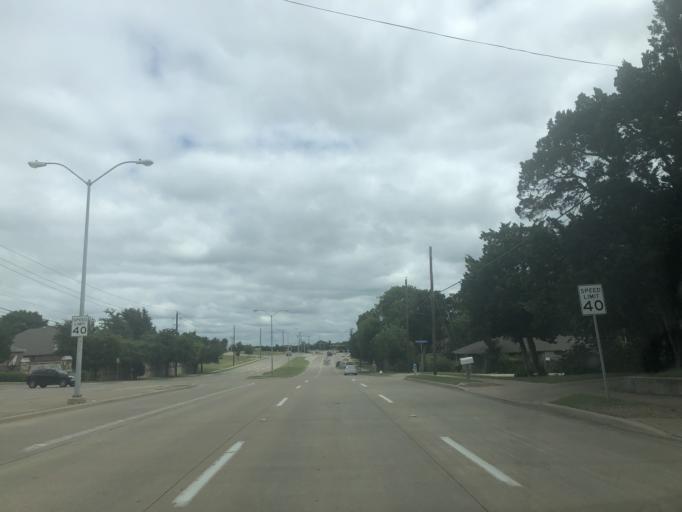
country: US
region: Texas
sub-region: Dallas County
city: Duncanville
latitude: 32.6586
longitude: -96.9430
